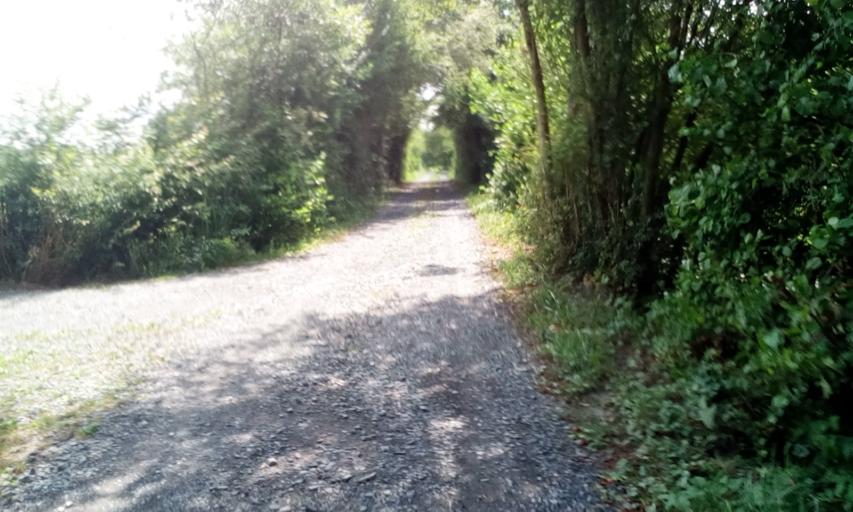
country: FR
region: Lower Normandy
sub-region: Departement du Calvados
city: Bavent
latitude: 49.2343
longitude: -0.1661
